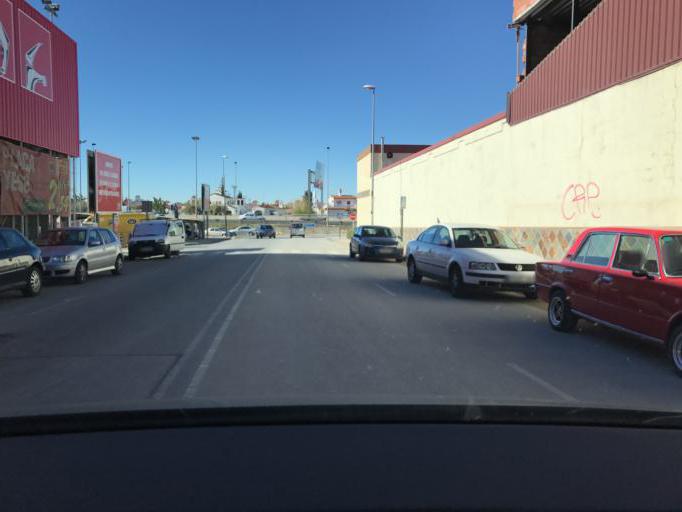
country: ES
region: Andalusia
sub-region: Provincia de Granada
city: Maracena
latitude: 37.2134
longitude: -3.6230
